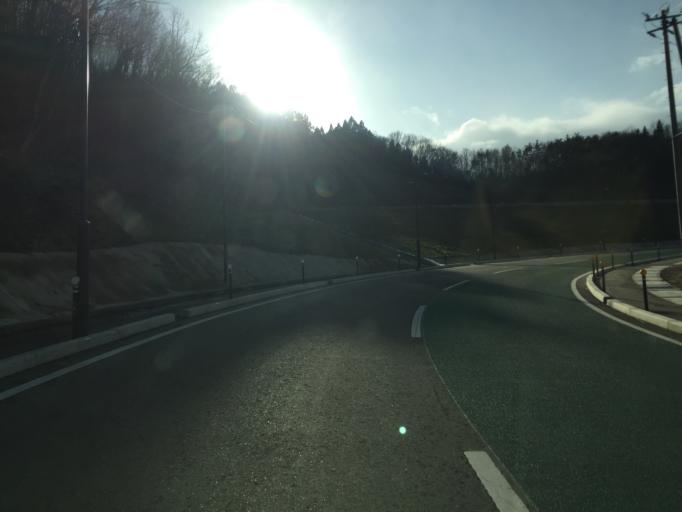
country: JP
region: Fukushima
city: Fukushima-shi
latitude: 37.6668
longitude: 140.5639
